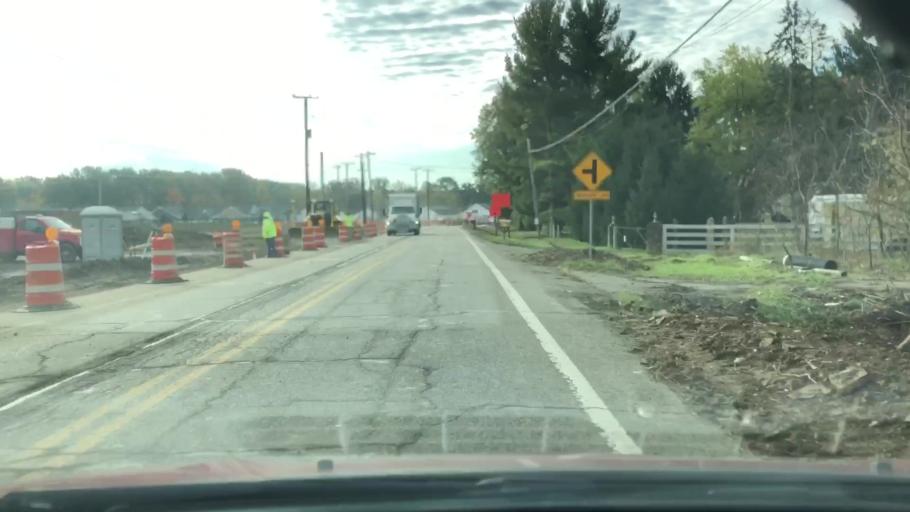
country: US
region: Ohio
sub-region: Franklin County
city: Huber Ridge
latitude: 40.0945
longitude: -82.8667
